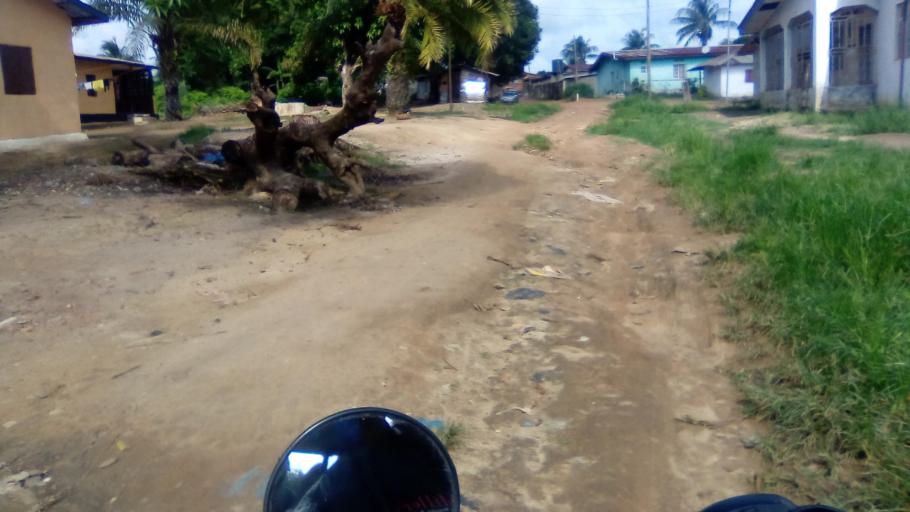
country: SL
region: Southern Province
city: Bo
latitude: 7.9587
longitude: -11.7541
